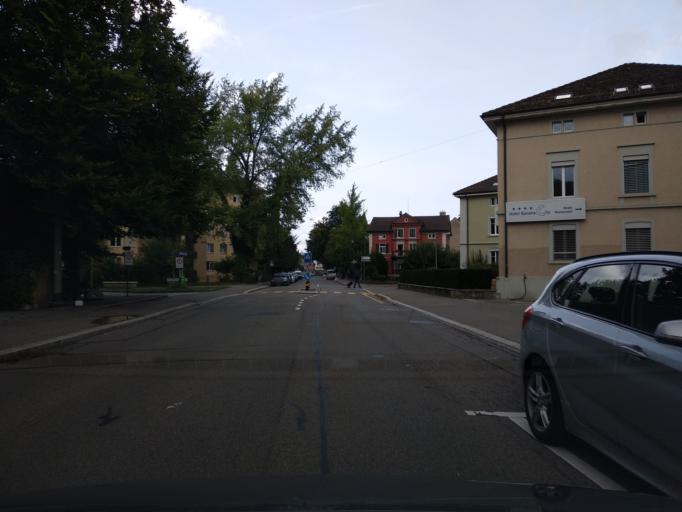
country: CH
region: Zurich
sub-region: Bezirk Winterthur
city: Winterthur
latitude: 47.5040
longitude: 8.7248
